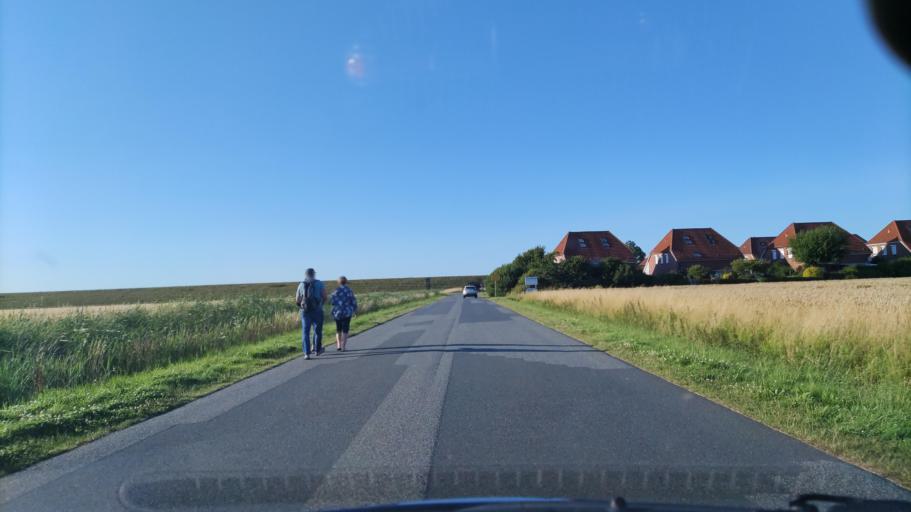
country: DE
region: Lower Saxony
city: Werdum
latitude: 53.7015
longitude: 7.8016
